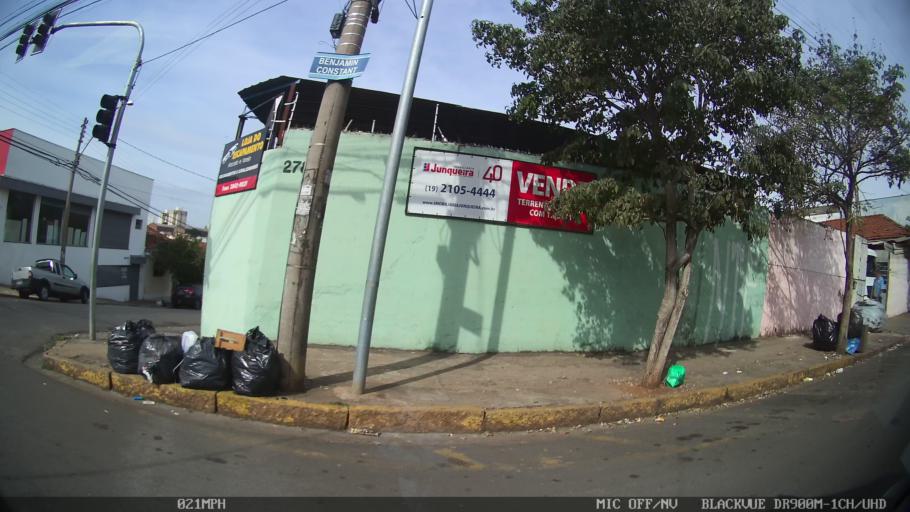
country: BR
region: Sao Paulo
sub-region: Piracicaba
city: Piracicaba
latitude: -22.7408
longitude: -47.6541
